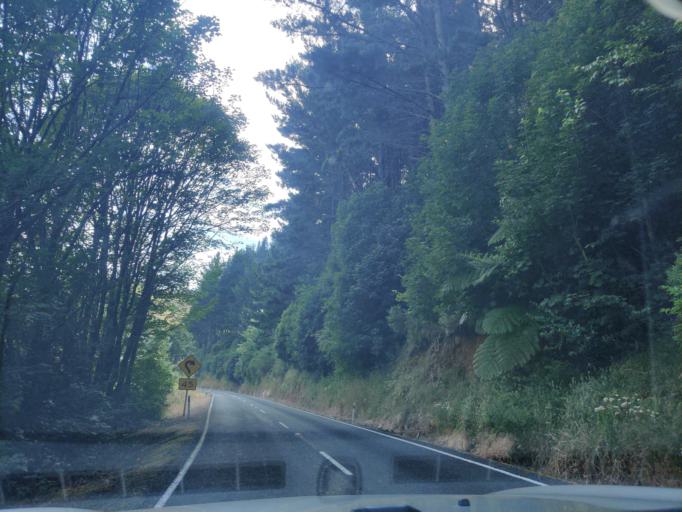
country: NZ
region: Waikato
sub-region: Otorohanga District
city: Otorohanga
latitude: -38.0978
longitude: 175.1233
